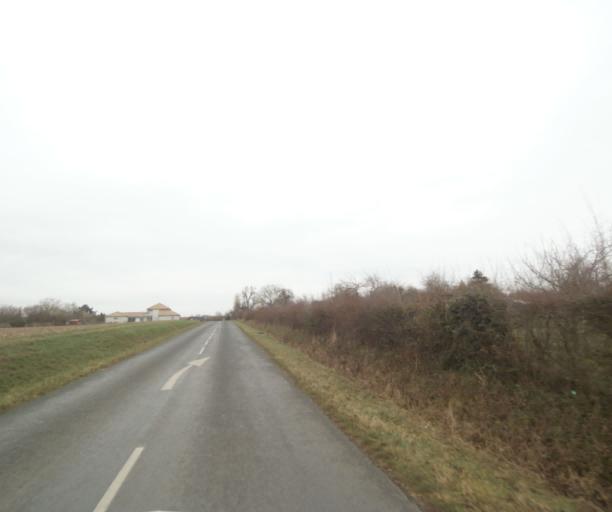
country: FR
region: Champagne-Ardenne
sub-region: Departement de la Haute-Marne
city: Villiers-en-Lieu
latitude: 48.6345
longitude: 4.7691
